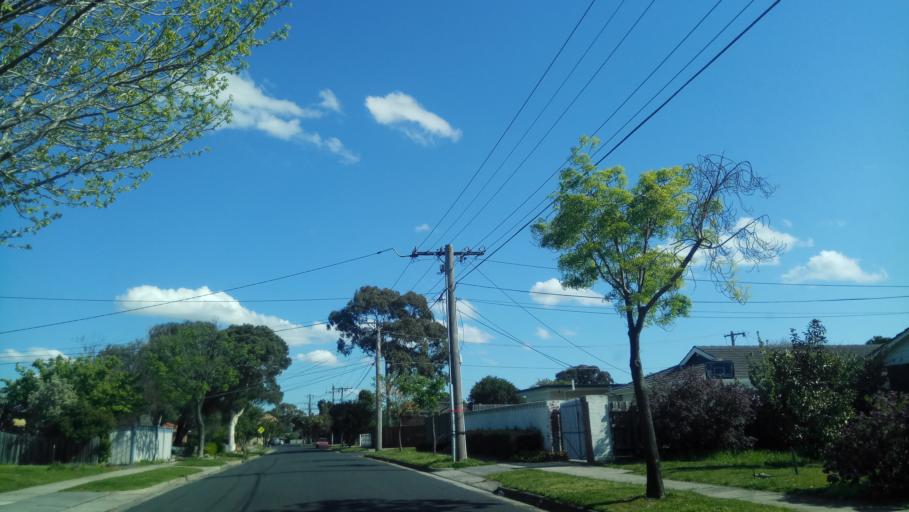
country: AU
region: Victoria
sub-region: Kingston
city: Dingley Village
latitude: -37.9819
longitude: 145.1270
